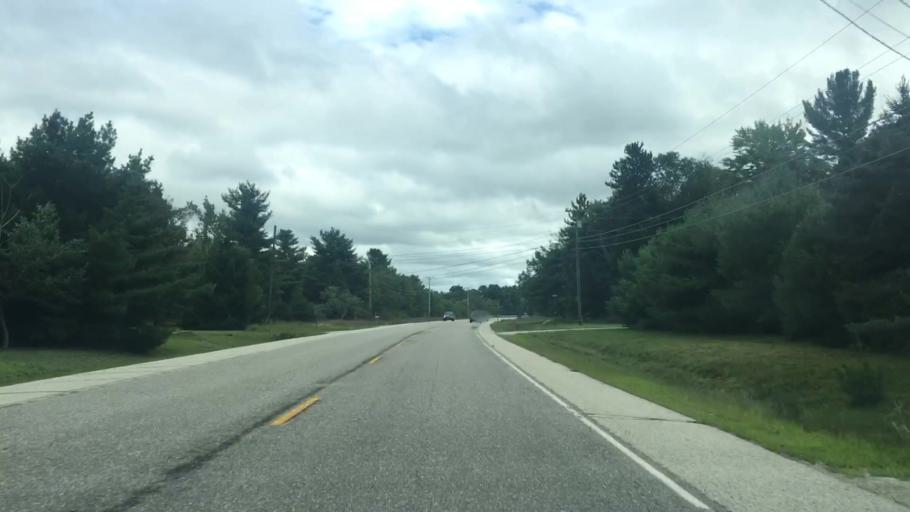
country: US
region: Maine
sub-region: York County
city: Lake Arrowhead
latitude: 43.6362
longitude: -70.7486
